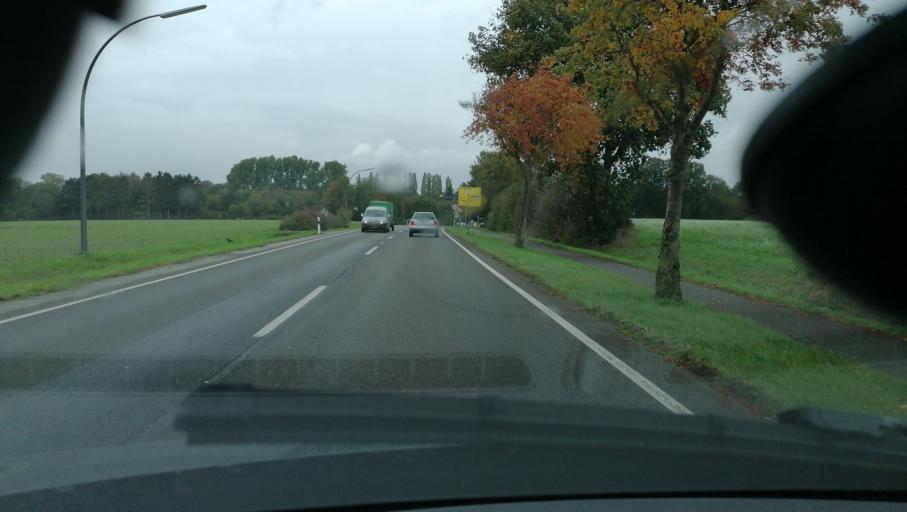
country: DE
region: North Rhine-Westphalia
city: Herten
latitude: 51.6243
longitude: 7.1590
